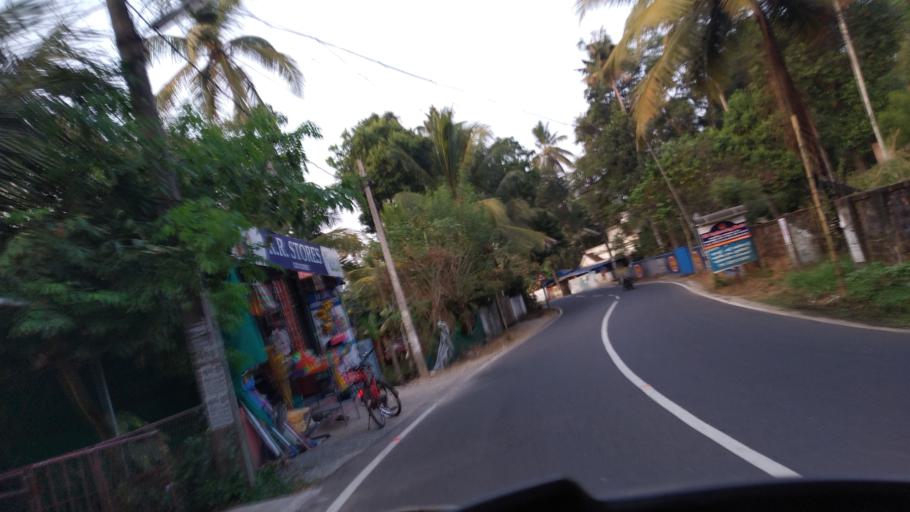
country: IN
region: Kerala
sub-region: Ernakulam
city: Elur
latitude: 10.1115
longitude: 76.2439
